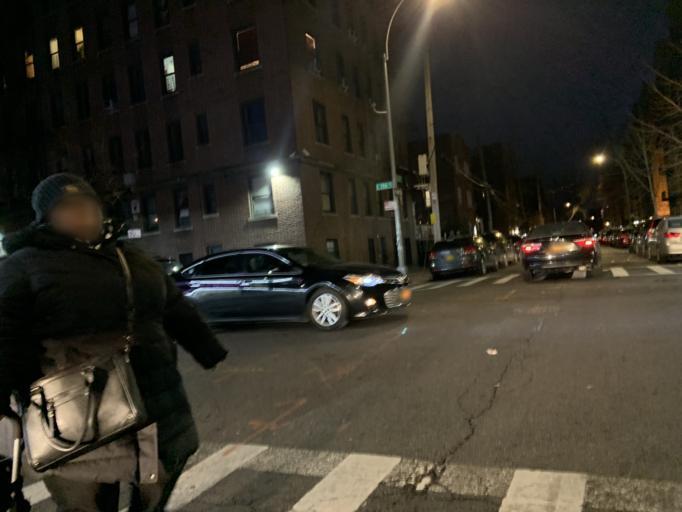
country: US
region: New York
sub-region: New York County
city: Inwood
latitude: 40.8685
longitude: -73.8941
